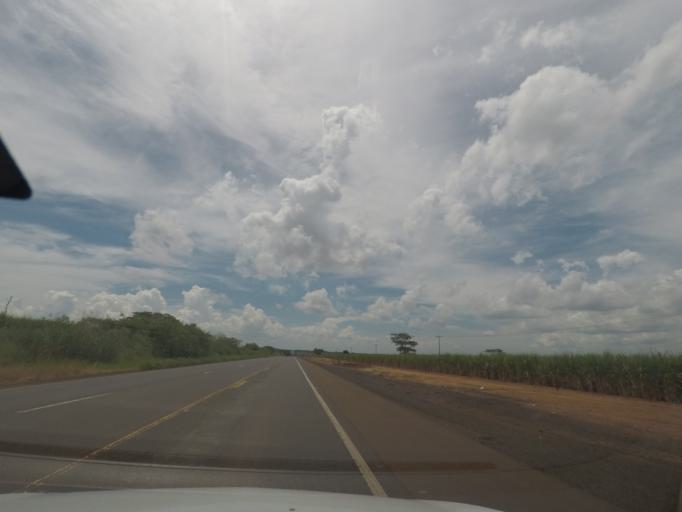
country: BR
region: Sao Paulo
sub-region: Barretos
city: Barretos
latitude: -20.3829
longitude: -48.6420
